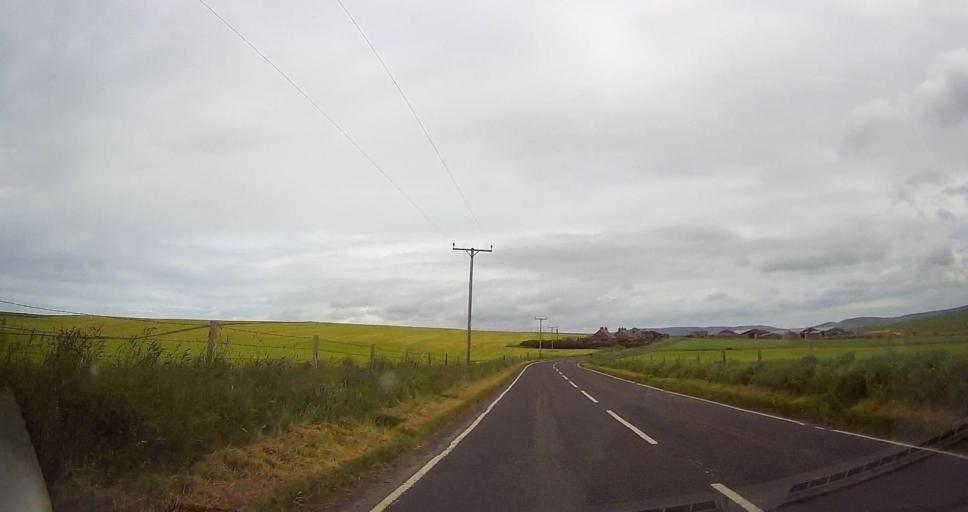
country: GB
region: Scotland
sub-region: Orkney Islands
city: Stromness
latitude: 58.9764
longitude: -3.2716
